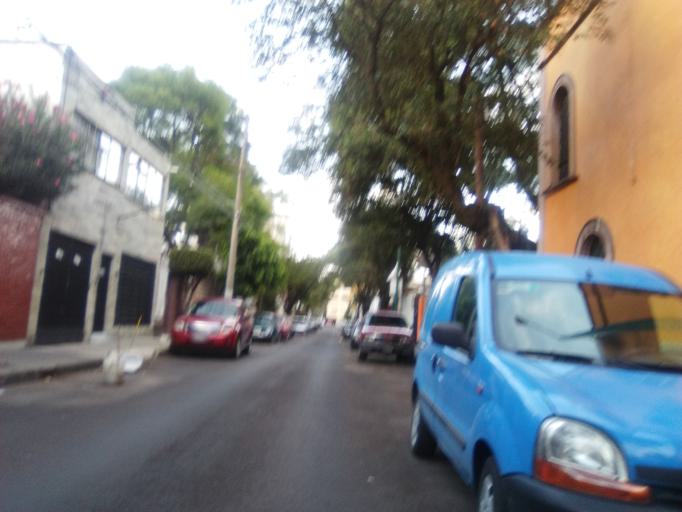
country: MX
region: Mexico City
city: Colonia del Valle
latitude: 19.3773
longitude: -99.1851
